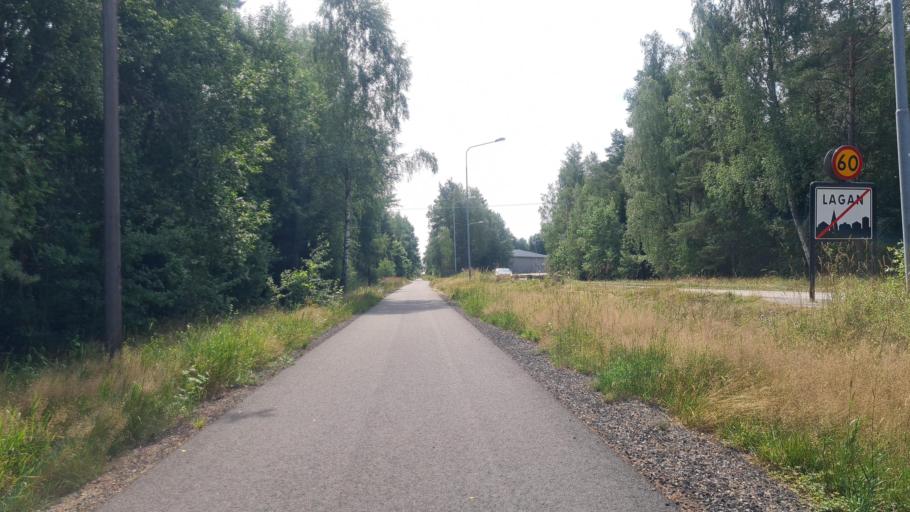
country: SE
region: Kronoberg
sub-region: Ljungby Kommun
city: Lagan
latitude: 56.9099
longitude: 13.9899
